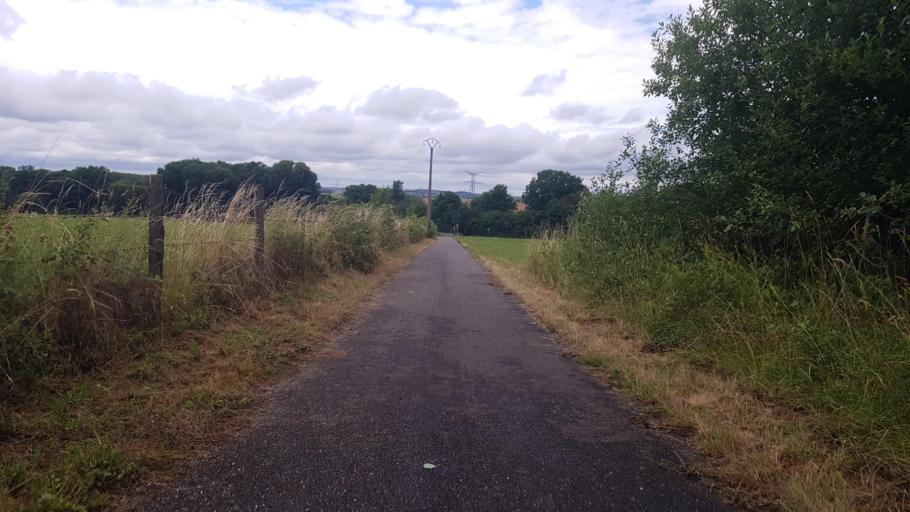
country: FR
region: Lorraine
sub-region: Departement de la Moselle
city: Niderviller
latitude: 48.7235
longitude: 7.1496
